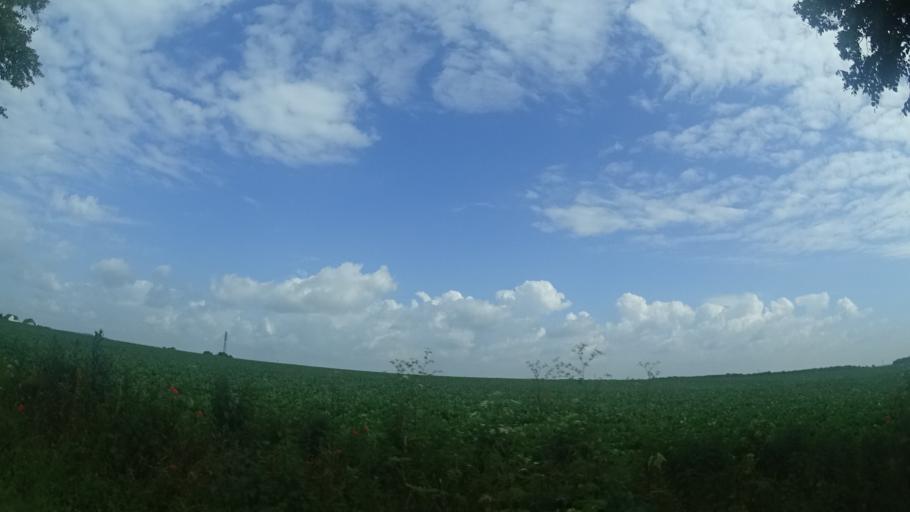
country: DE
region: Lower Saxony
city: Pattensen
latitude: 52.2101
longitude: 9.7205
